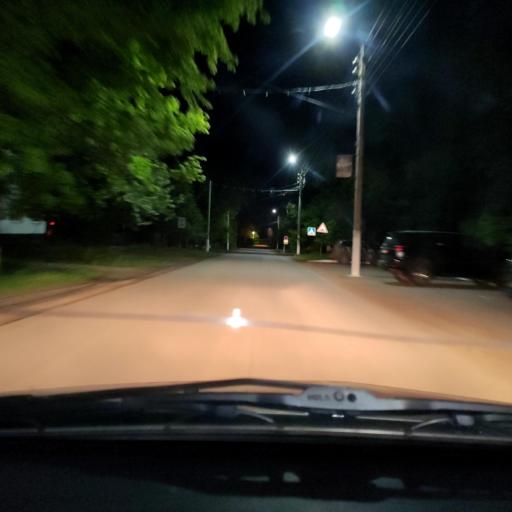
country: RU
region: Bashkortostan
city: Avdon
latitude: 54.6569
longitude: 55.5968
